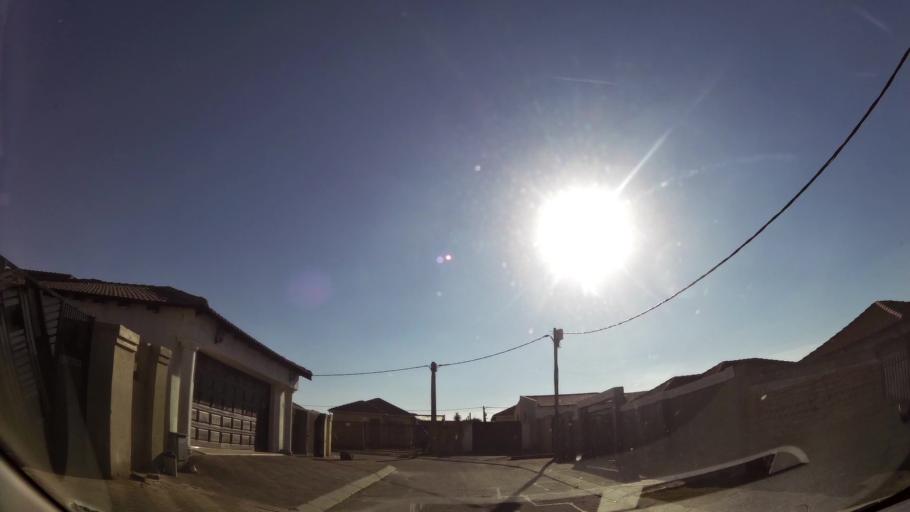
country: ZA
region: Gauteng
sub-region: City of Johannesburg Metropolitan Municipality
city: Johannesburg
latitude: -26.2078
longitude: 27.9717
